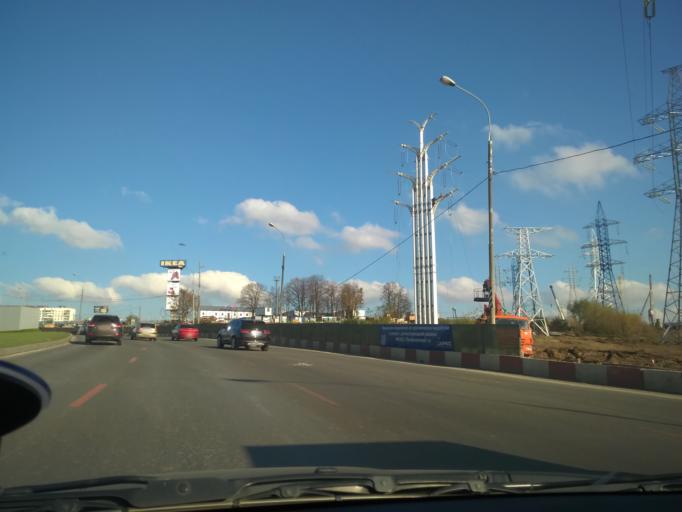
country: RU
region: Moscow
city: Tyoply Stan
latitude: 55.6083
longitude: 37.4889
